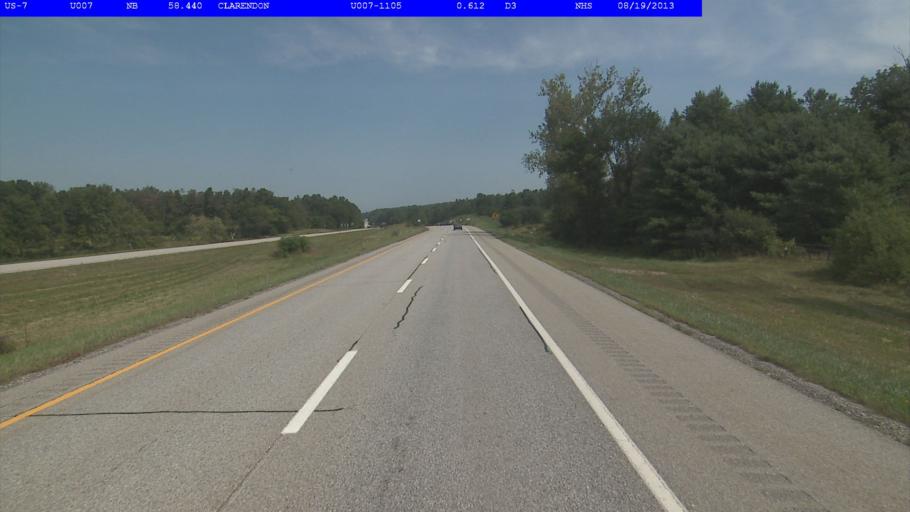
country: US
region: Vermont
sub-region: Rutland County
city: Rutland
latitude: 43.5028
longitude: -72.9674
